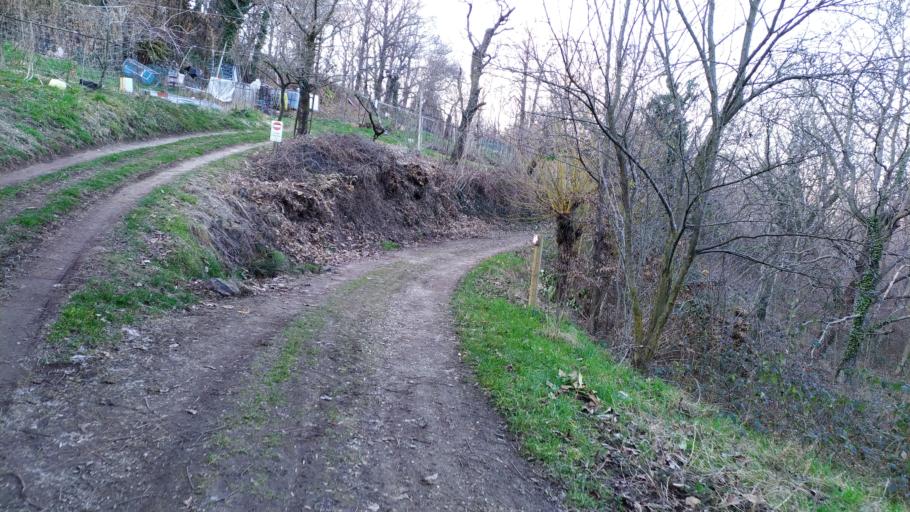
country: IT
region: Veneto
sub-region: Provincia di Vicenza
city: Monte di Malo
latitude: 45.6669
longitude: 11.3501
